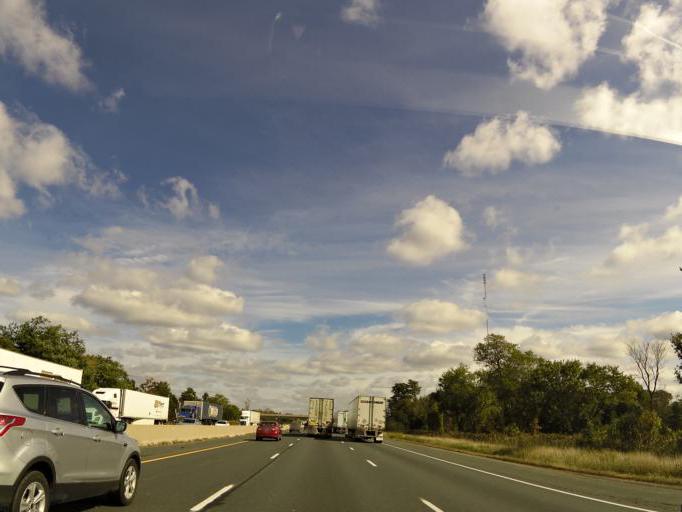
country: CA
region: Ontario
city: Dorchester
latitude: 42.9416
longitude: -81.1401
